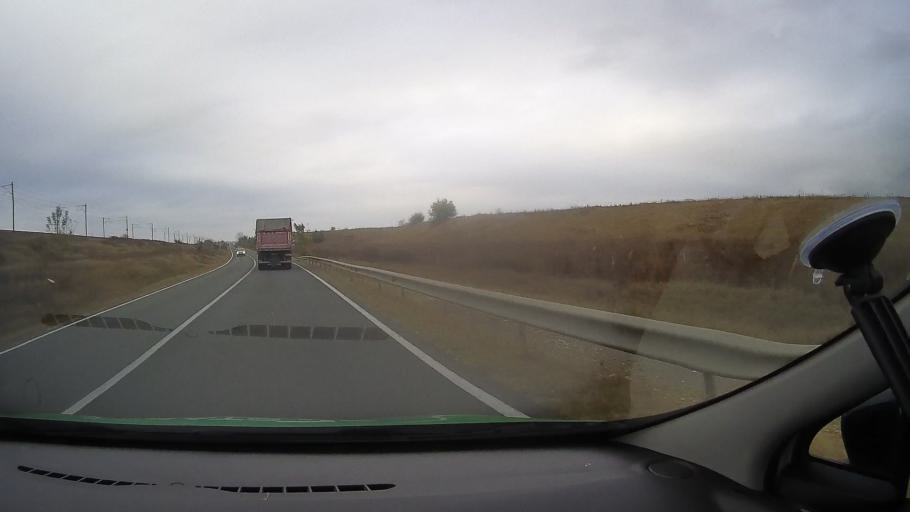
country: RO
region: Constanta
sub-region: Comuna Poarta Alba
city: Poarta Alba
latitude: 44.2220
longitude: 28.3868
